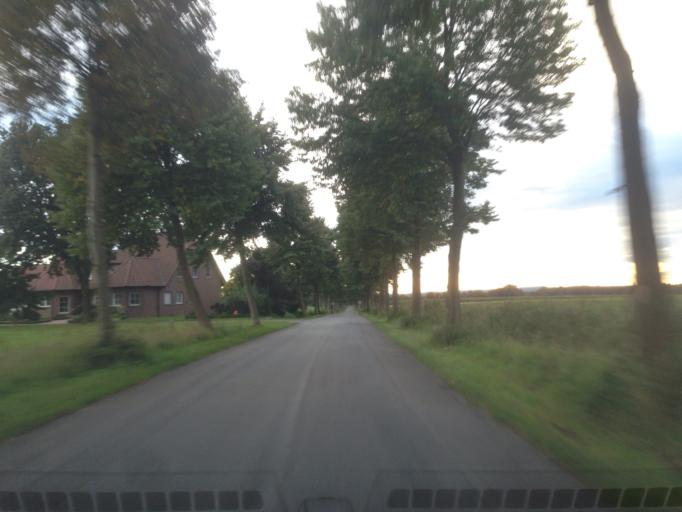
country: DE
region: North Rhine-Westphalia
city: Olfen
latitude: 51.7483
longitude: 7.3899
